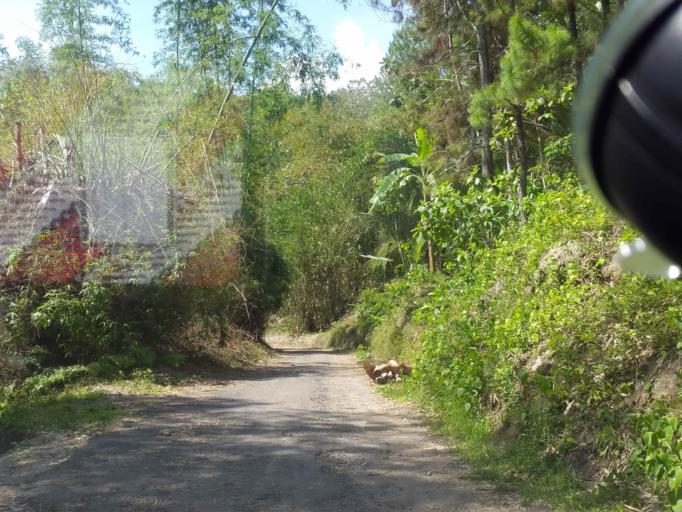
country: ID
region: East Java
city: Prambonkrajan
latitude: -8.0013
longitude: 111.6872
